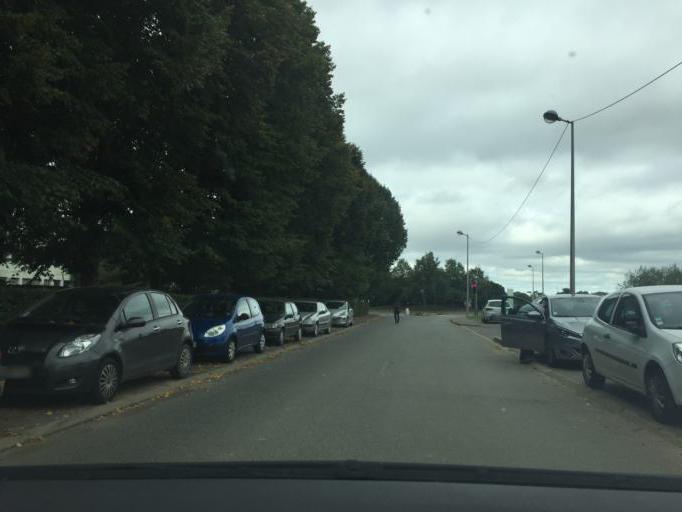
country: FR
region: Ile-de-France
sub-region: Departement de l'Essonne
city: Bures-sur-Yvette
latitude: 48.7107
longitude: 2.1722
